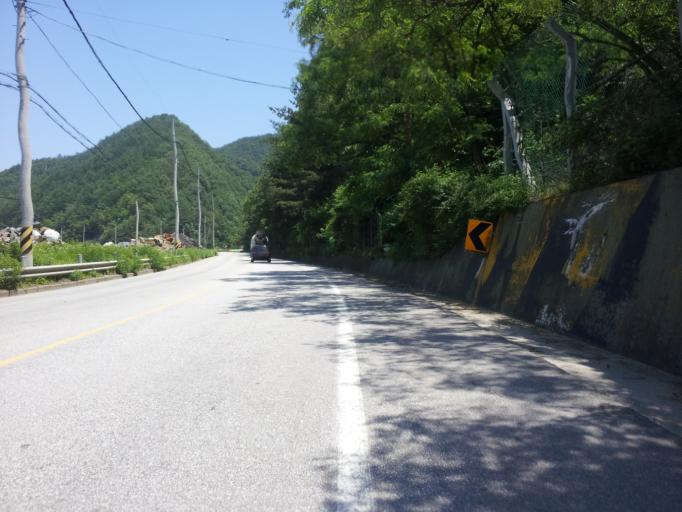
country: KR
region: Chungcheongbuk-do
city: Okcheon
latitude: 36.3682
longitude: 127.6399
